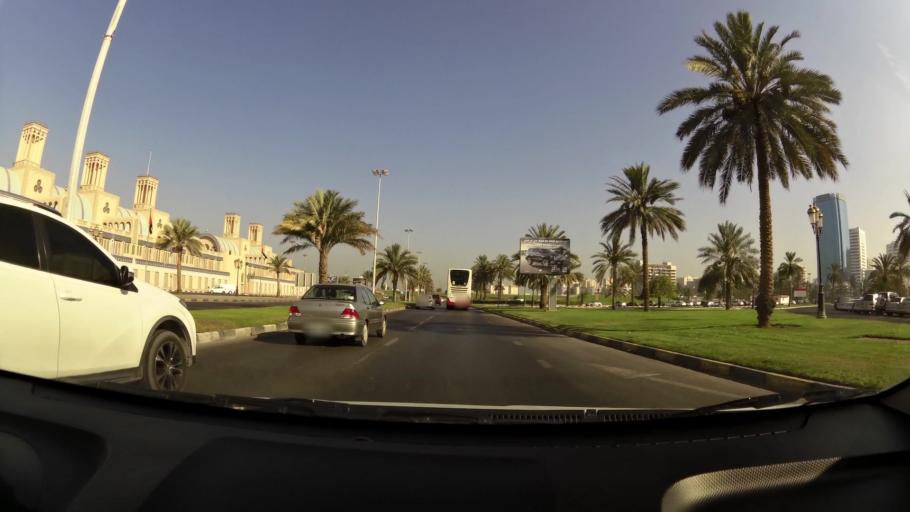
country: AE
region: Ash Shariqah
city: Sharjah
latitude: 25.3476
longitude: 55.3848
